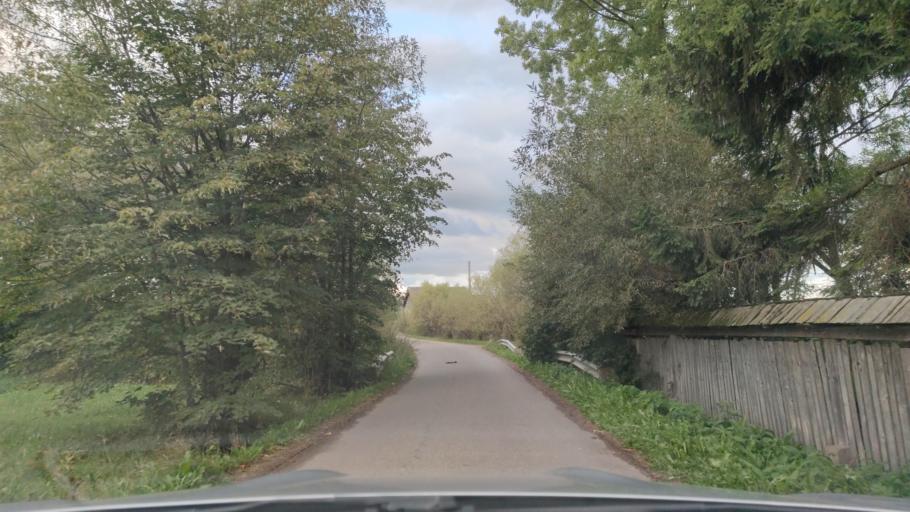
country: RO
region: Harghita
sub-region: Comuna Remetea
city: Remetea
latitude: 46.8102
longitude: 25.4365
